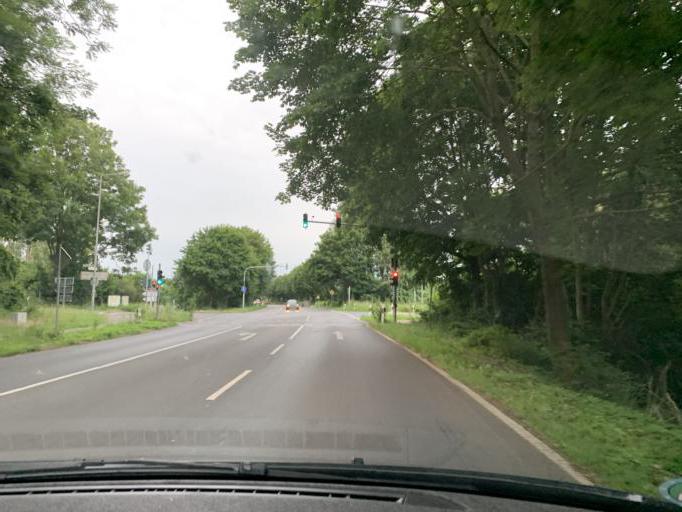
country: DE
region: North Rhine-Westphalia
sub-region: Regierungsbezirk Koln
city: Kerpen
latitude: 50.8844
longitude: 6.7184
